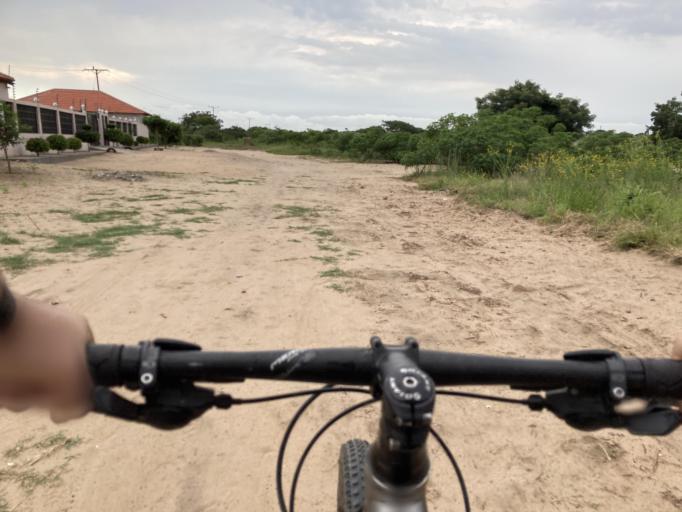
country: MZ
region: Maputo City
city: Maputo
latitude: -26.0529
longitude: 32.5351
